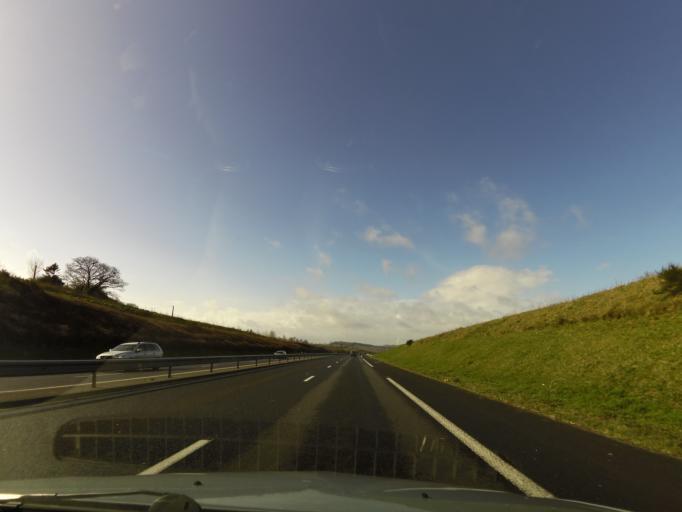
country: FR
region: Lower Normandy
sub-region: Departement de la Manche
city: Saint-Amand
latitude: 48.9986
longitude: -0.9129
